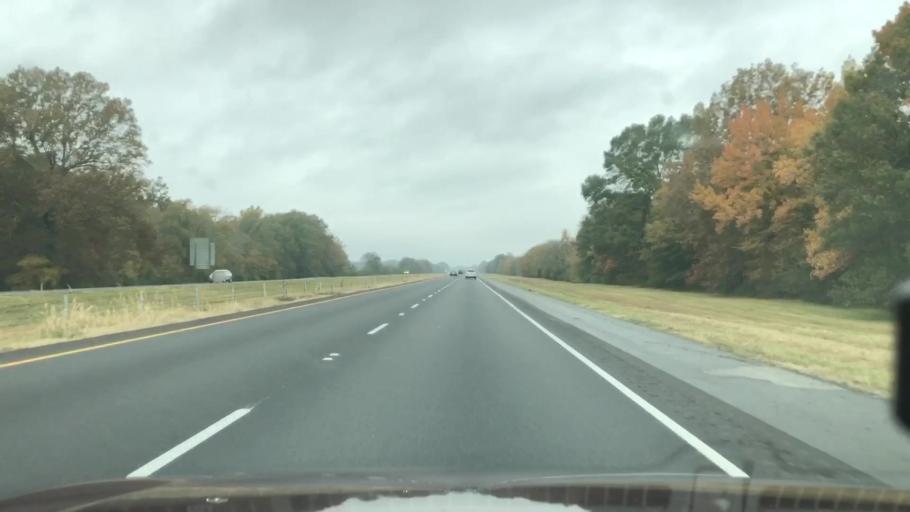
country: US
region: Louisiana
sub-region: Richland Parish
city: Rayville
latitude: 32.4602
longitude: -91.7781
